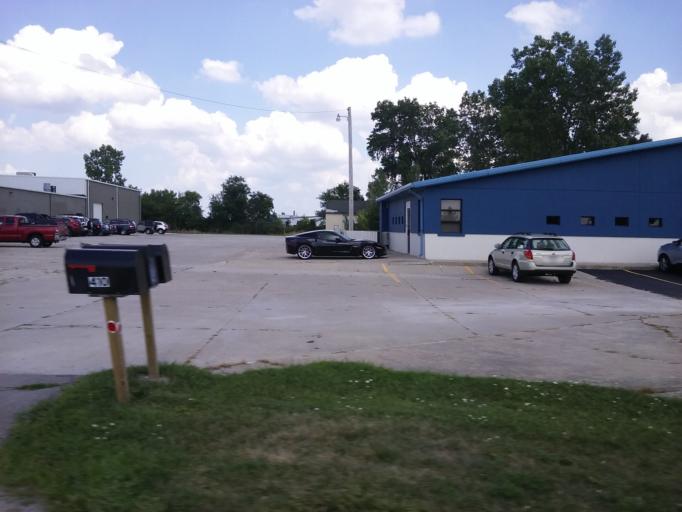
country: US
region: Ohio
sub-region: Wood County
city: Bowling Green
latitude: 41.3784
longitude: -83.6103
